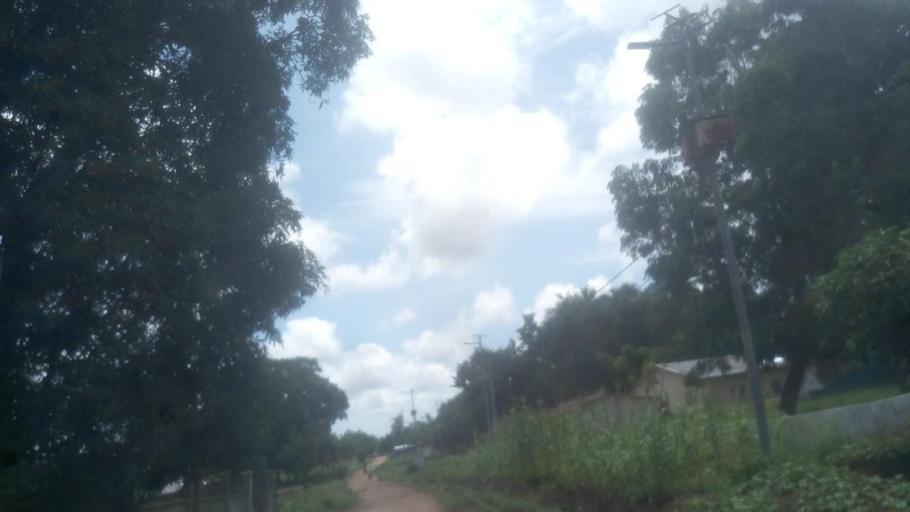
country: SL
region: Northern Province
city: Masoyila
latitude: 8.6036
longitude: -13.1989
